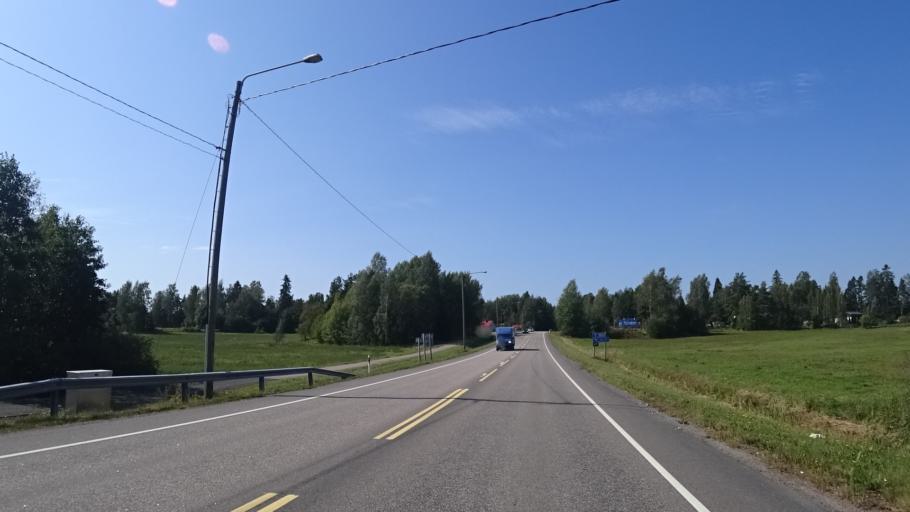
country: FI
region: Kymenlaakso
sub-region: Kotka-Hamina
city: Karhula
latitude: 60.5620
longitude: 27.0419
